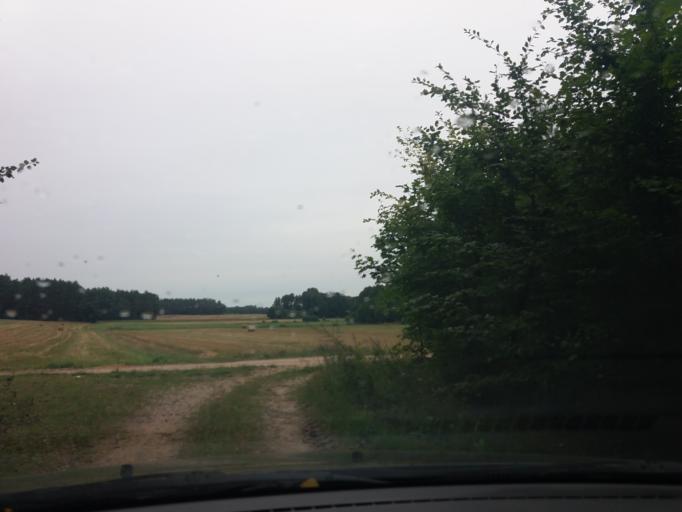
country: PL
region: Masovian Voivodeship
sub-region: Powiat mlawski
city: Wieczfnia Koscielna
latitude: 53.2339
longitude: 20.4833
